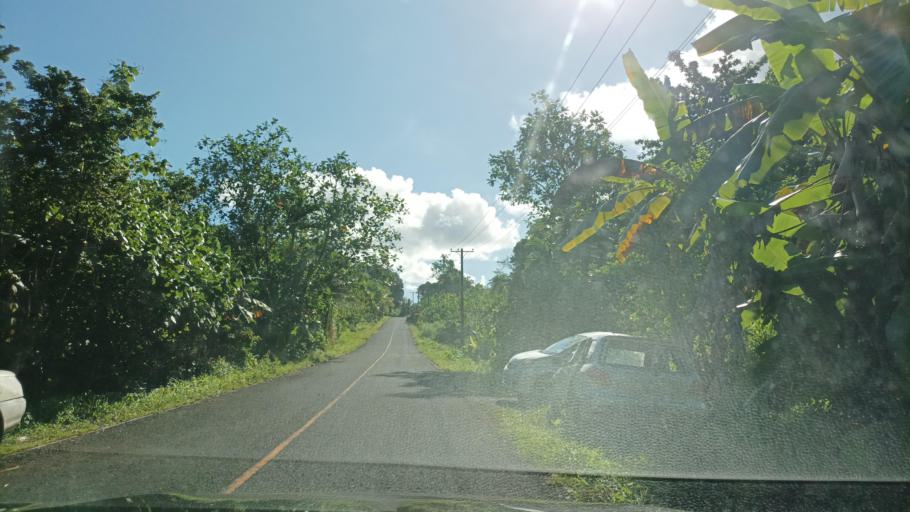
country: FM
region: Pohnpei
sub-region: Madolenihm Municipality
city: Madolenihm Municipality Government
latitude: 6.8085
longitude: 158.2827
